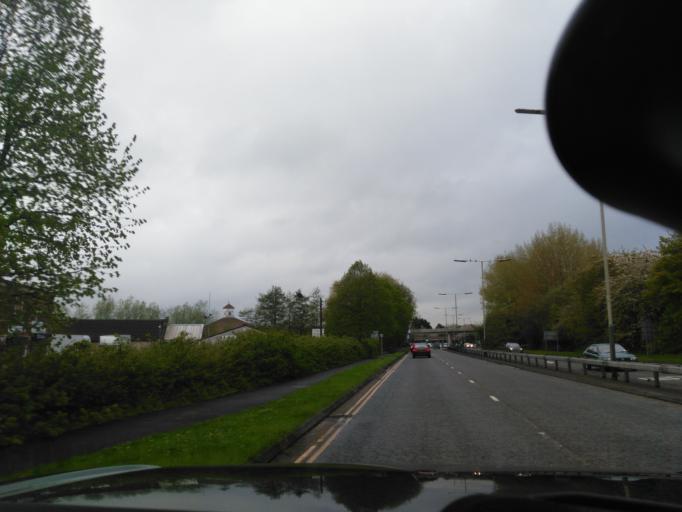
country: GB
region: England
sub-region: Wiltshire
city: Trowbridge
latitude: 51.3187
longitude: -2.2017
